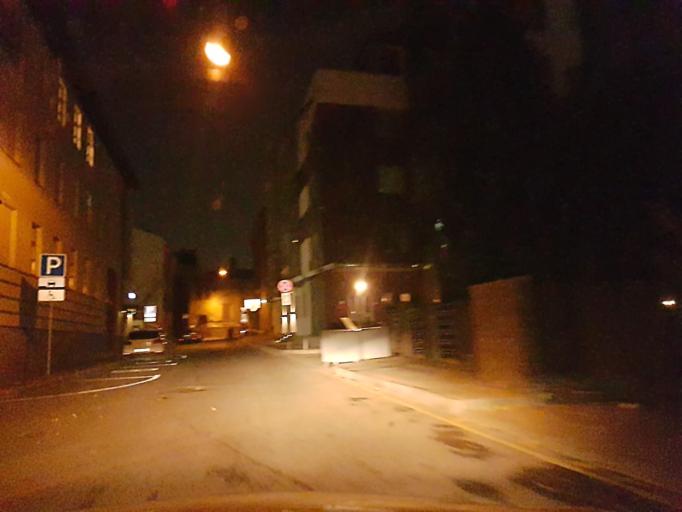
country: RU
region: Moscow
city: Moscow
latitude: 55.7392
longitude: 37.5999
